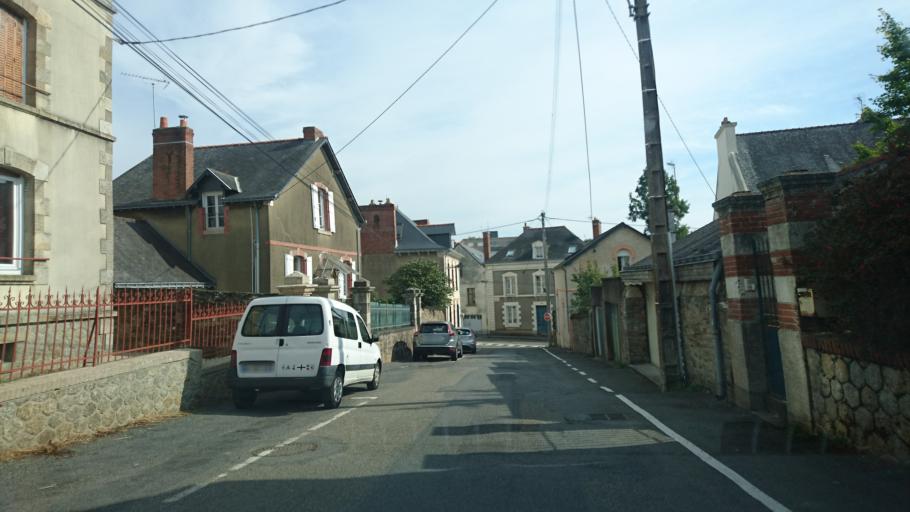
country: FR
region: Brittany
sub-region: Departement d'Ille-et-Vilaine
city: Redon
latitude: 47.6538
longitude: -2.0860
